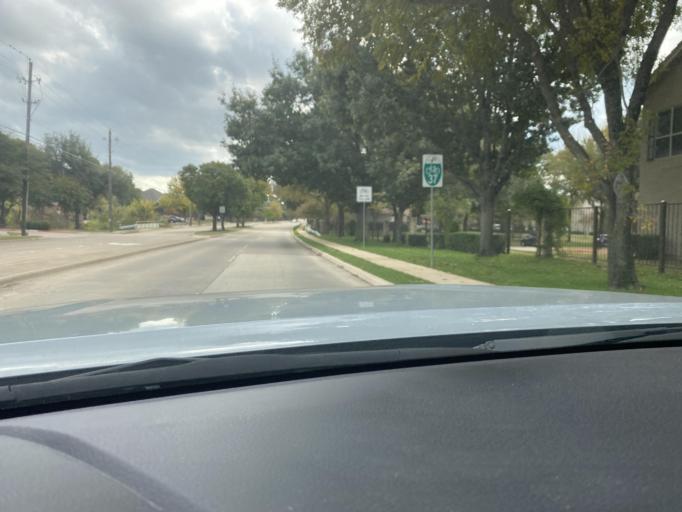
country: US
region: Texas
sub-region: Collin County
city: Frisco
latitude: 33.0705
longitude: -96.7919
